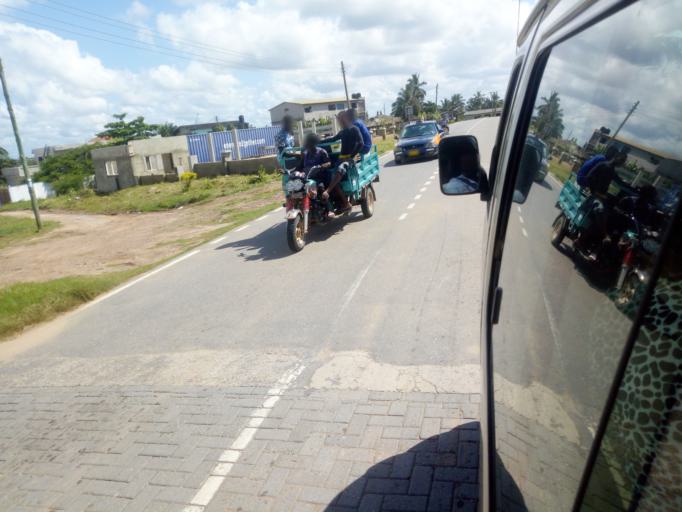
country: GH
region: Central
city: Elmina
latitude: 5.0943
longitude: -1.3367
